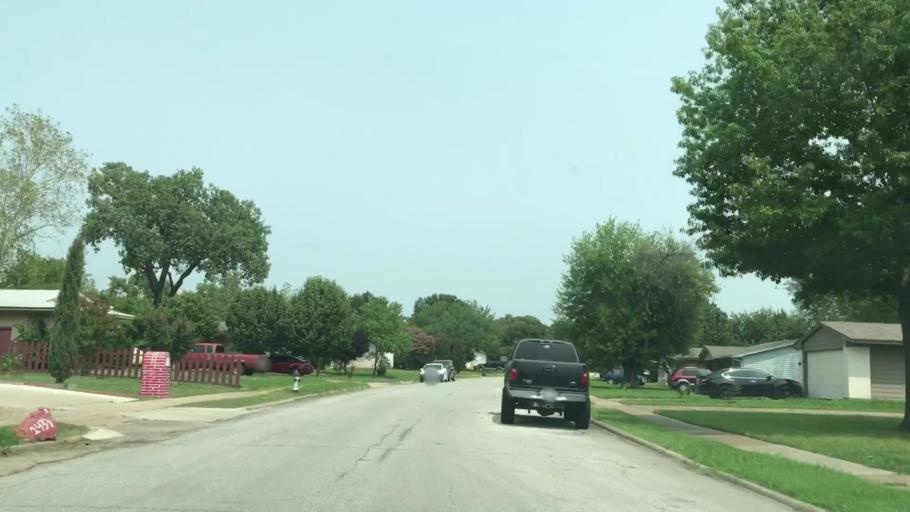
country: US
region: Texas
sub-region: Dallas County
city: Irving
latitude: 32.8475
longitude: -96.9788
